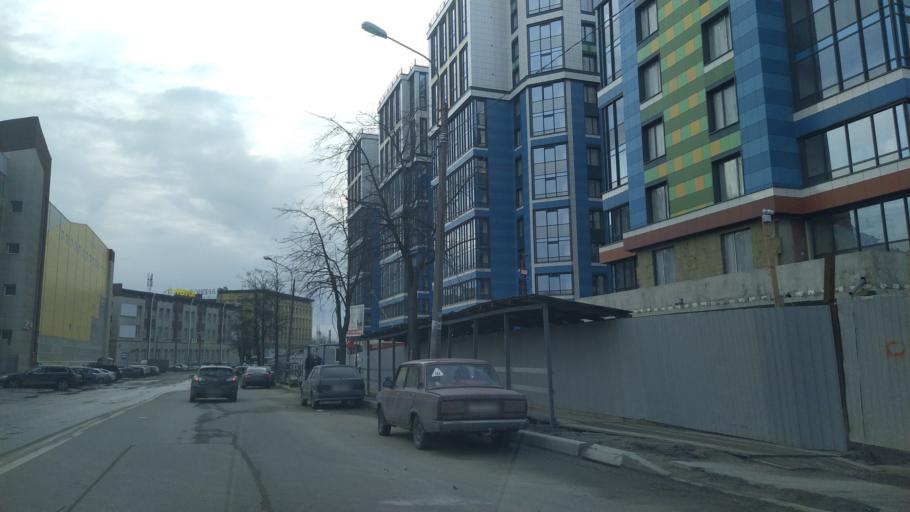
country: RU
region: St.-Petersburg
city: Kushelevka
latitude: 59.9827
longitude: 30.3596
